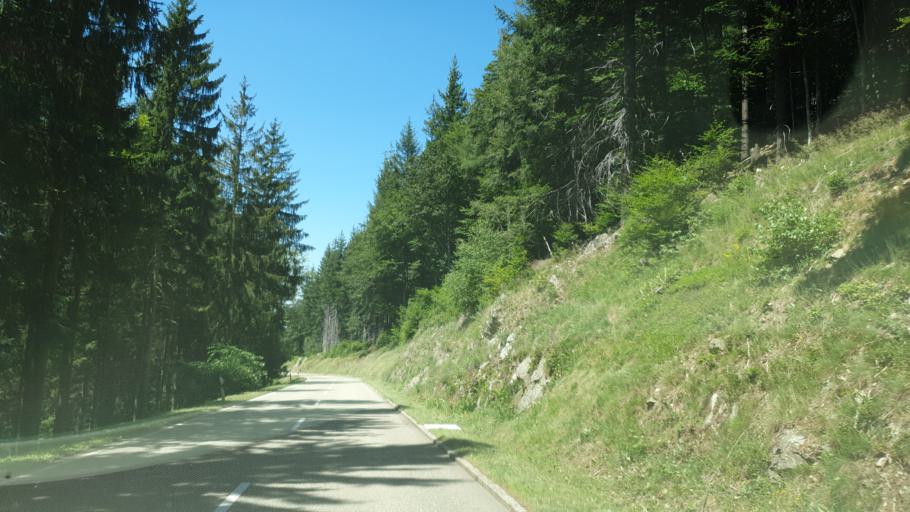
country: DE
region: Baden-Wuerttemberg
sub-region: Freiburg Region
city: Horben
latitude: 47.9159
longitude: 7.8759
